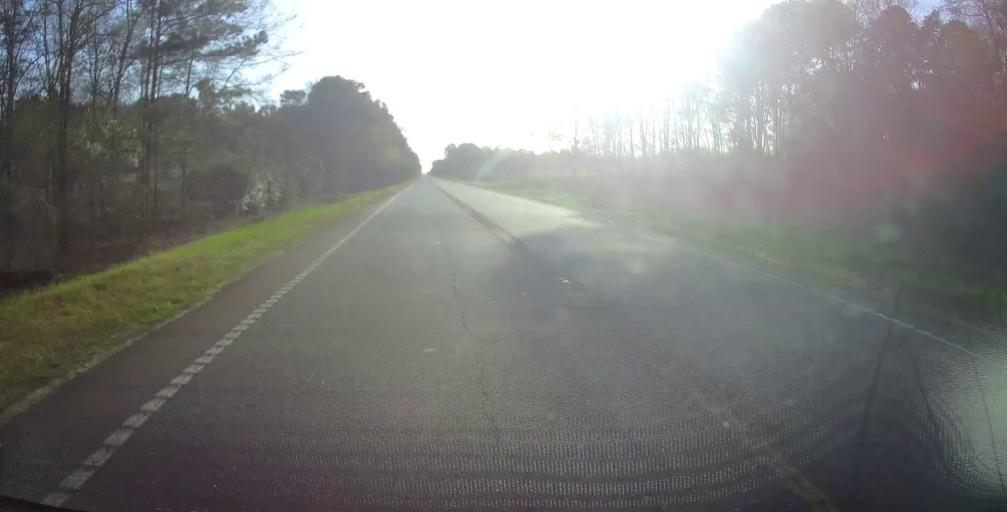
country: US
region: Georgia
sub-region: Tattnall County
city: Reidsville
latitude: 32.1291
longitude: -82.0531
